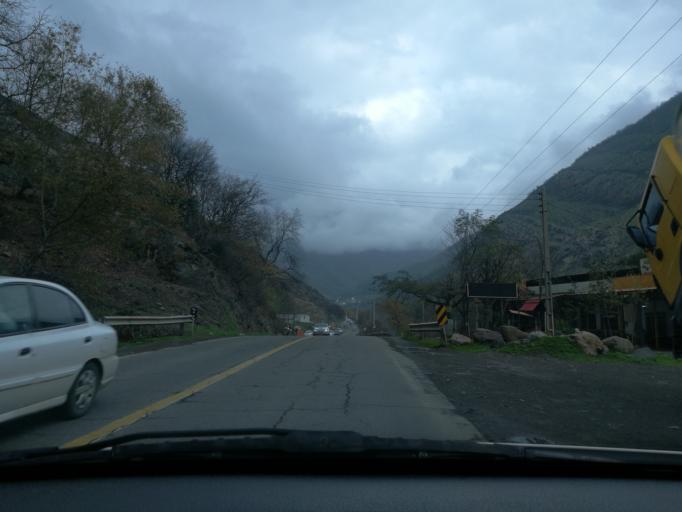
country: IR
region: Mazandaran
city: Chalus
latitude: 36.3692
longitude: 51.2648
